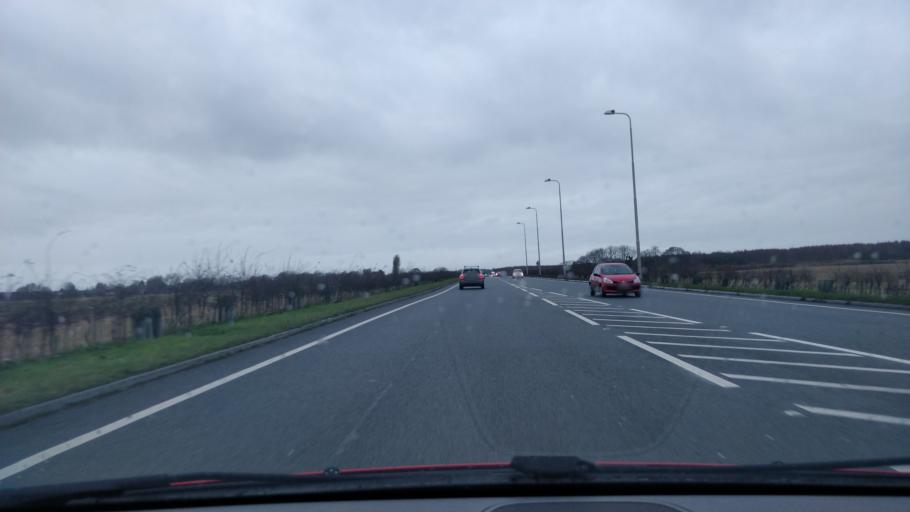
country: GB
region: England
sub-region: Sefton
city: Thornton
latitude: 53.4985
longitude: -2.9824
